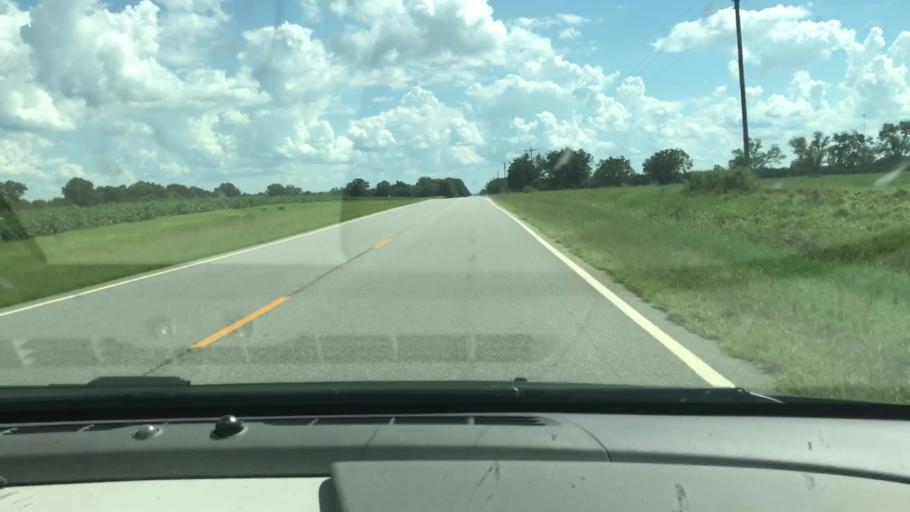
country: US
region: Georgia
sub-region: Quitman County
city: Georgetown
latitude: 31.8086
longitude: -85.0933
